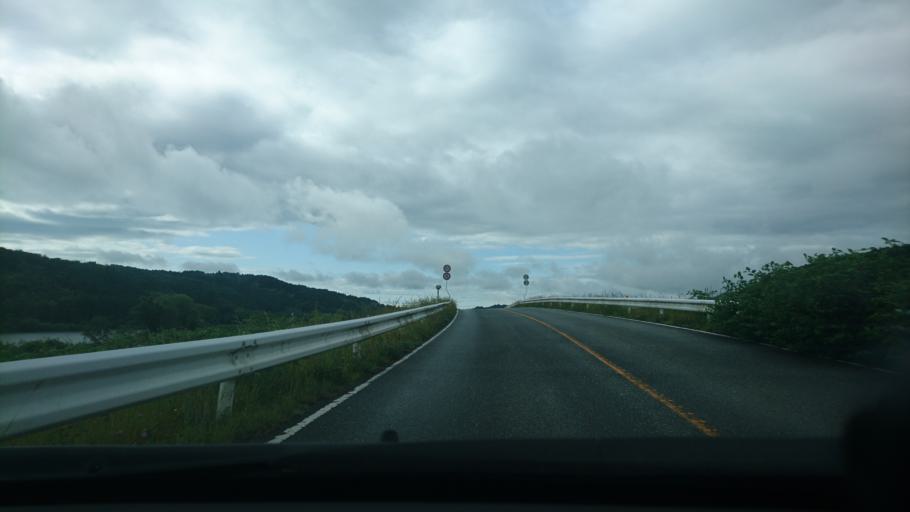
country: JP
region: Miyagi
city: Wakuya
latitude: 38.6338
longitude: 141.2899
